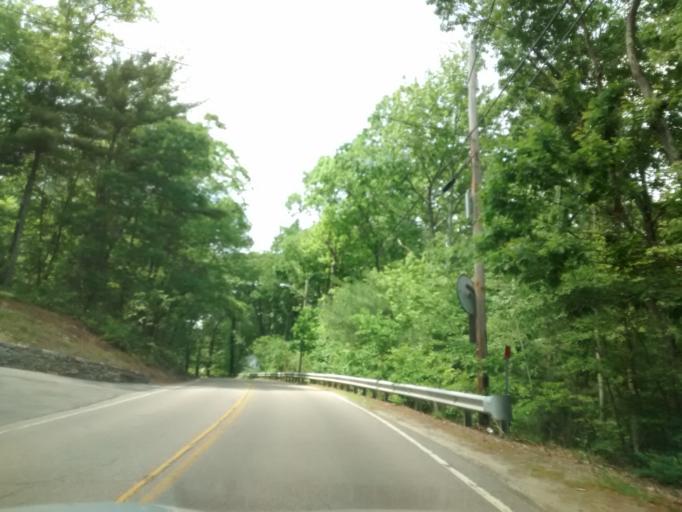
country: US
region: Massachusetts
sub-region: Worcester County
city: Whitinsville
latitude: 42.1209
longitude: -71.6902
